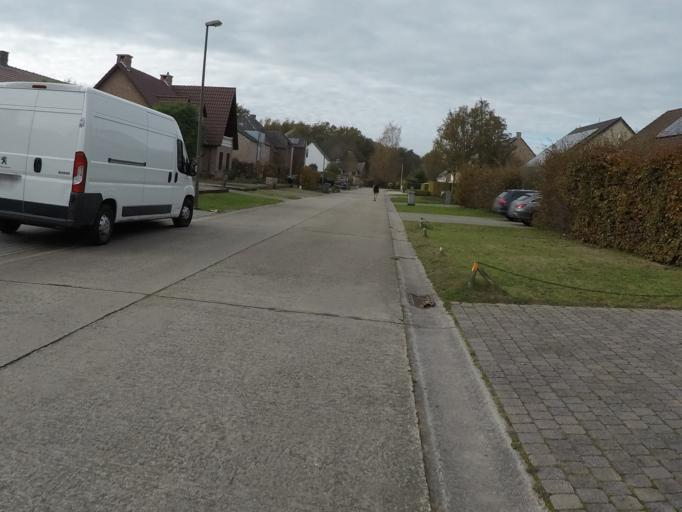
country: BE
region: Flanders
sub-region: Provincie Antwerpen
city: Nijlen
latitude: 51.1561
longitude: 4.6541
